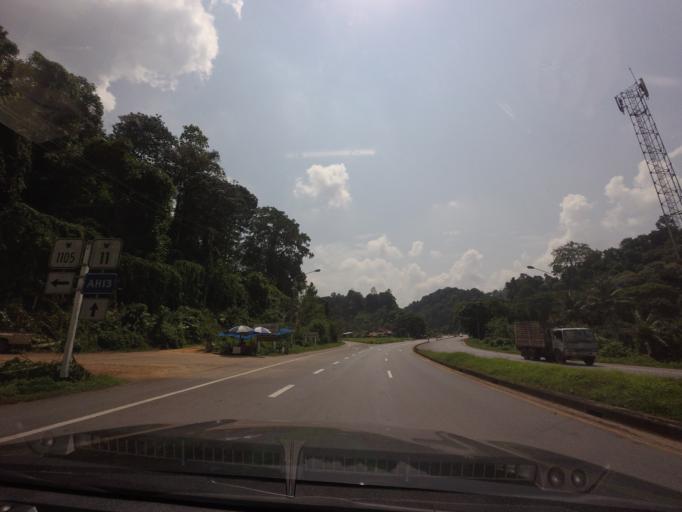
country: TH
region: Uttaradit
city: Lap Lae
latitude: 17.8094
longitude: 100.1085
